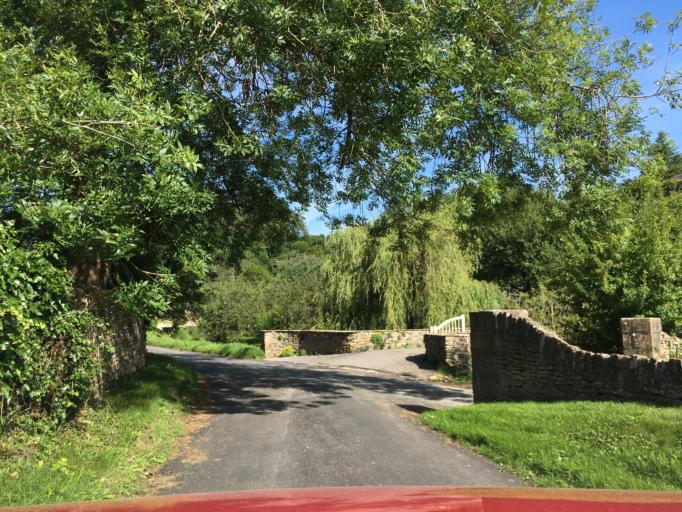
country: GB
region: England
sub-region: Wiltshire
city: Nettleton
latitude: 51.4953
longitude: -2.2717
